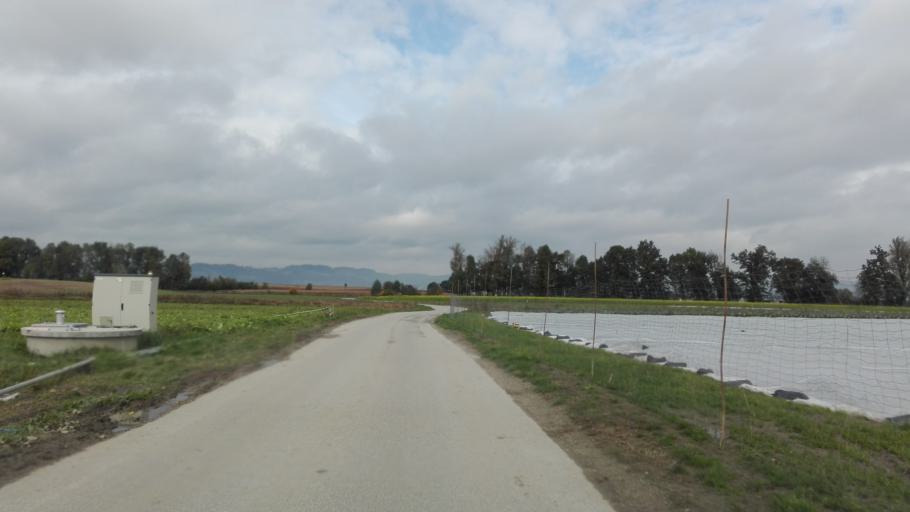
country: AT
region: Upper Austria
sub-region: Politischer Bezirk Urfahr-Umgebung
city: Feldkirchen an der Donau
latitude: 48.3264
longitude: 14.0003
